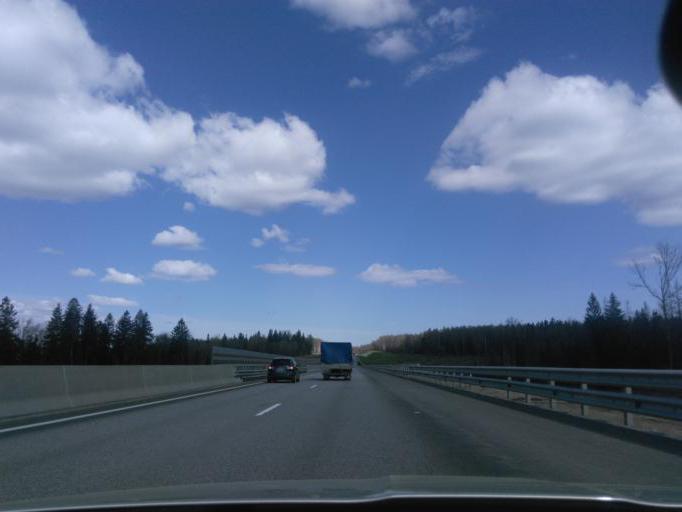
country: RU
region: Moskovskaya
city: Lozhki
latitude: 56.1207
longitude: 37.1145
